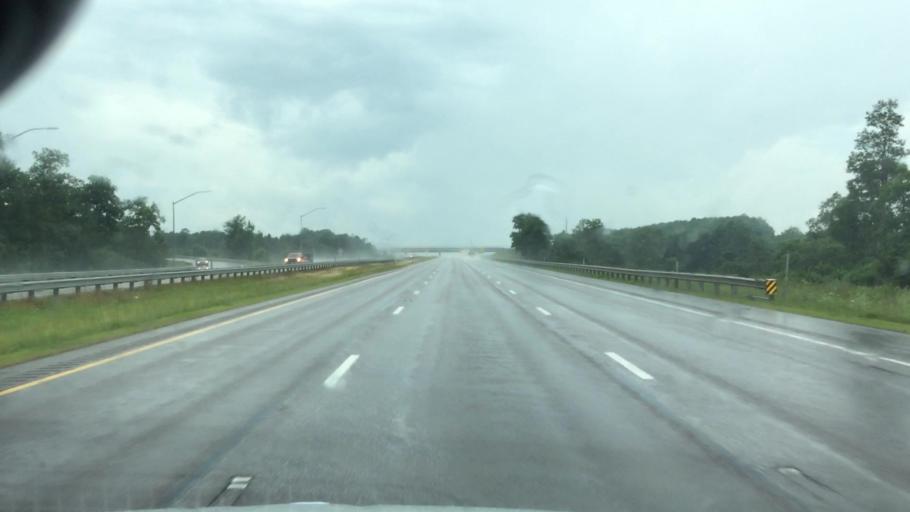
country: US
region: Pennsylvania
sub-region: Somerset County
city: Meyersdale
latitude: 39.6854
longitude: -79.2433
